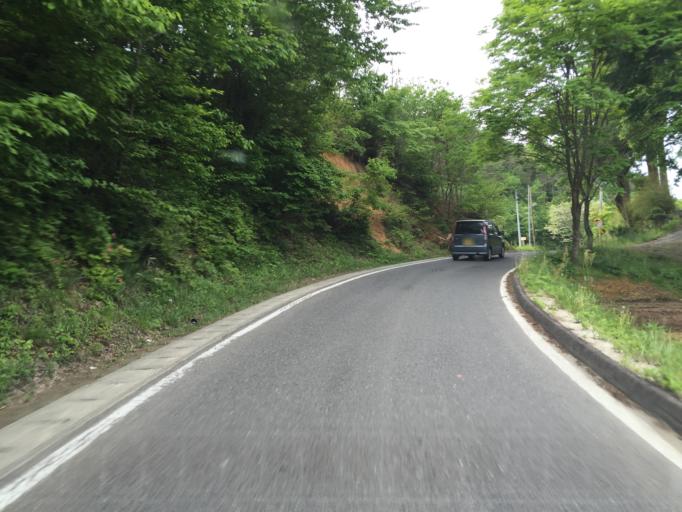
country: JP
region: Fukushima
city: Fukushima-shi
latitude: 37.6872
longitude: 140.5734
